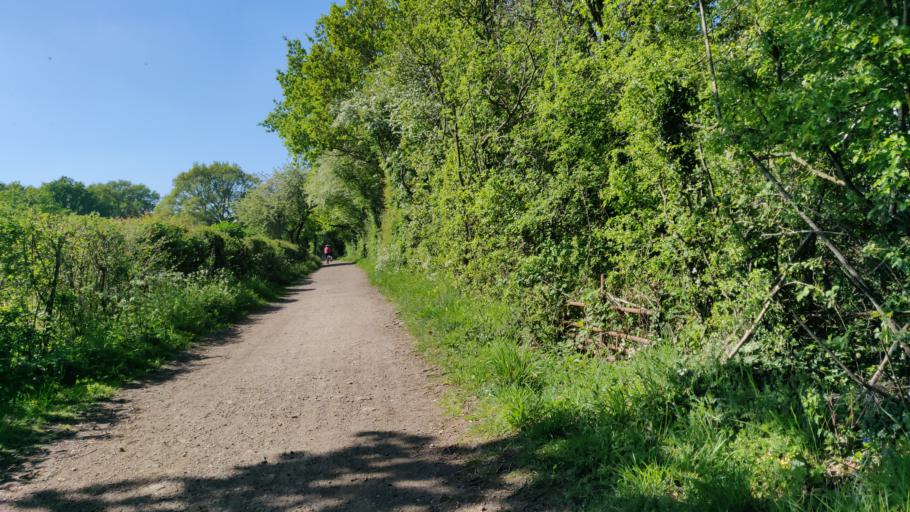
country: GB
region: England
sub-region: West Sussex
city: Southwater
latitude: 51.0596
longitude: -0.3844
